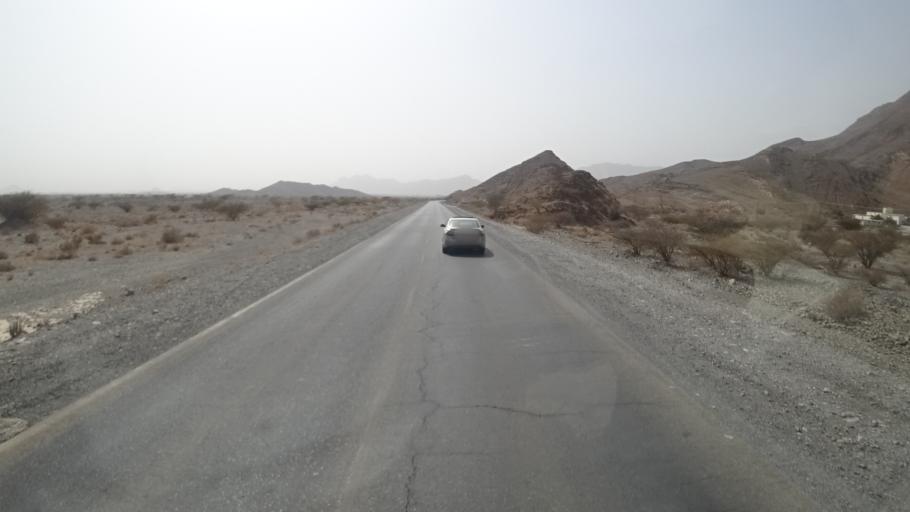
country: OM
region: Muhafazat ad Dakhiliyah
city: Izki
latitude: 22.9250
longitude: 57.6523
